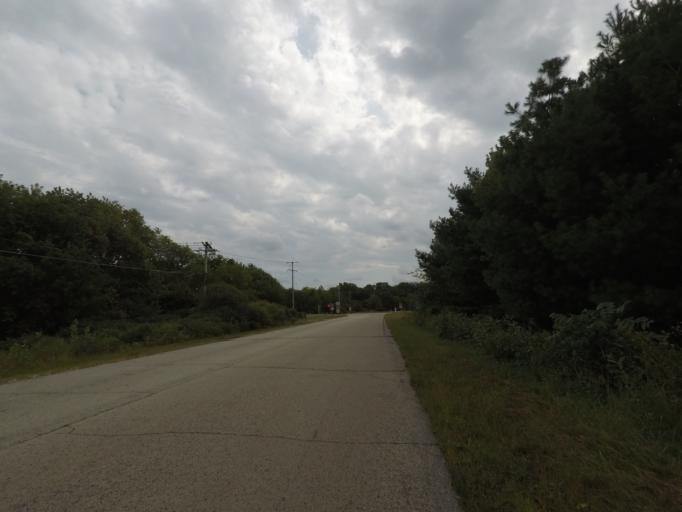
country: US
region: Wisconsin
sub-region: Jefferson County
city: Fort Atkinson
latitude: 42.8922
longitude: -88.8687
